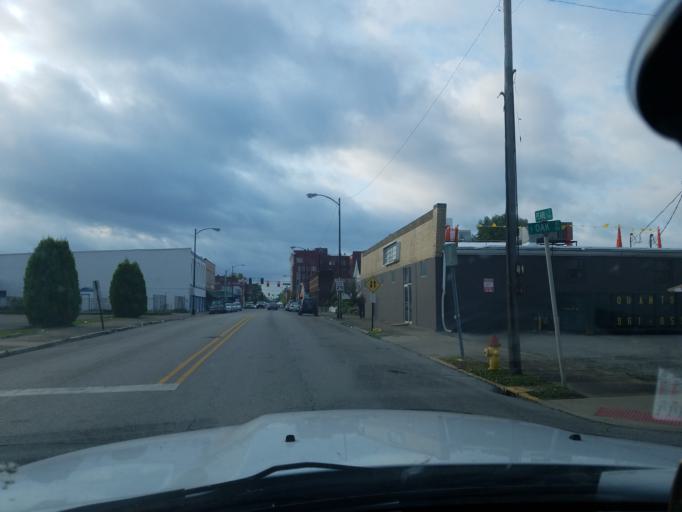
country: US
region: Indiana
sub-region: Floyd County
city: New Albany
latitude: 38.2881
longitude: -85.8241
